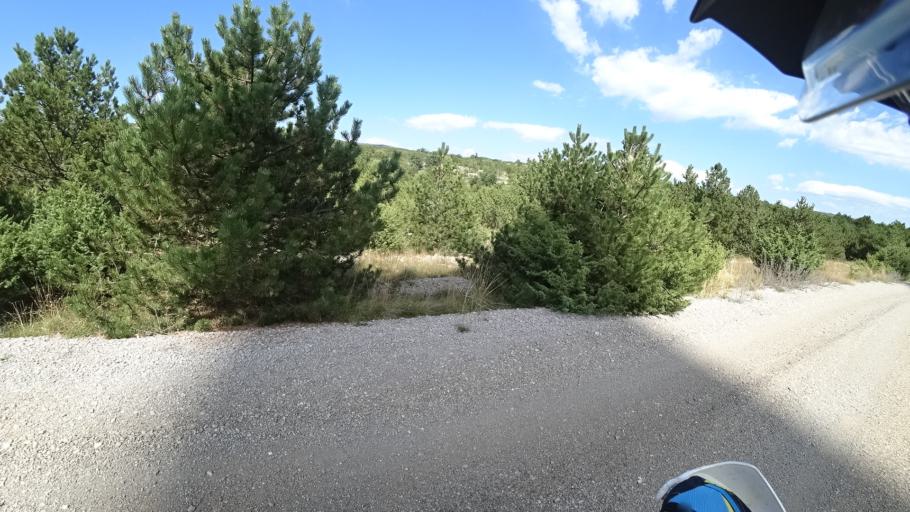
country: HR
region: Splitsko-Dalmatinska
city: Hrvace
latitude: 43.7198
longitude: 16.5292
